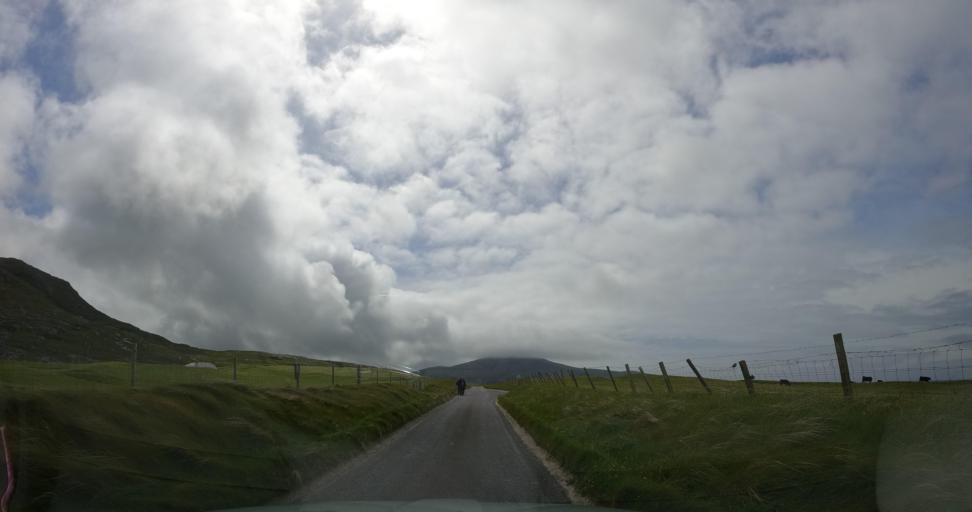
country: GB
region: Scotland
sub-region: Eilean Siar
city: Barra
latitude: 56.9966
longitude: -7.5063
